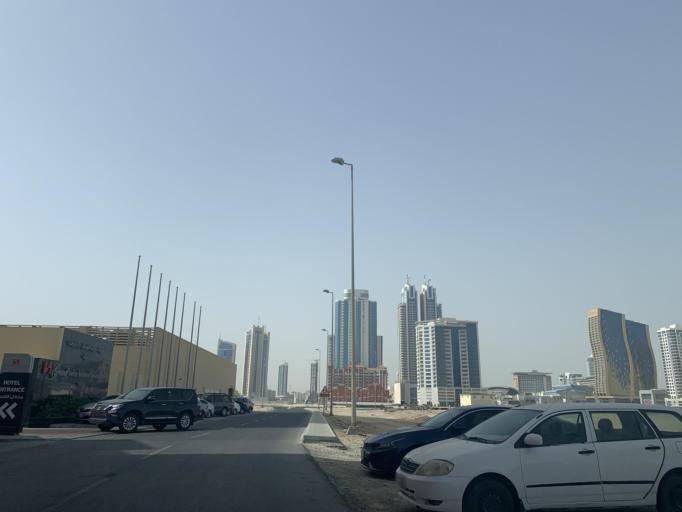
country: BH
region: Manama
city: Jidd Hafs
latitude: 26.2424
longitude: 50.5572
